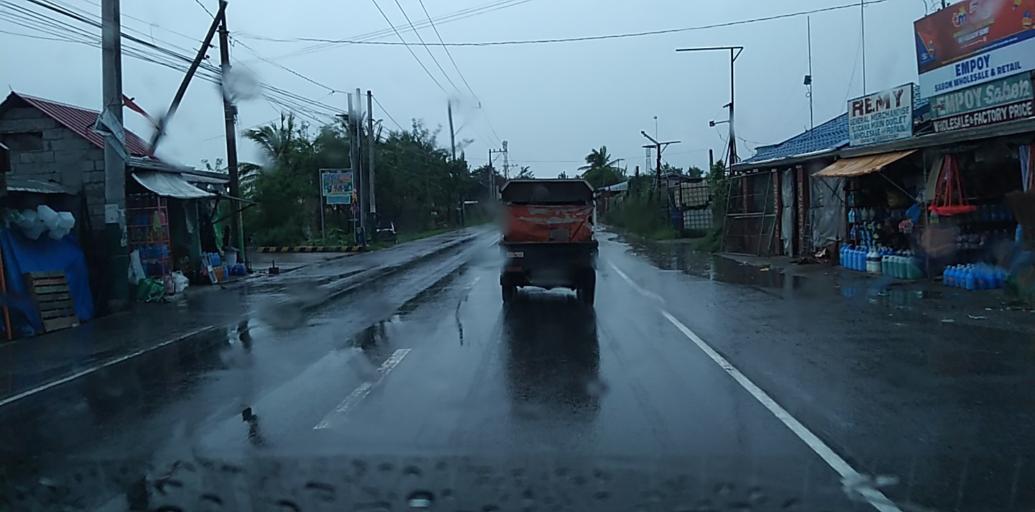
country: PH
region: Central Luzon
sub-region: Province of Bulacan
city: Bulualto
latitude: 15.2130
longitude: 120.9554
